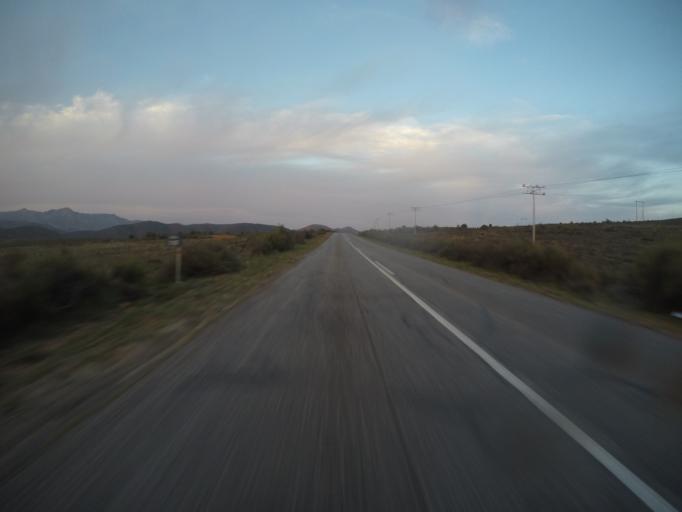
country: ZA
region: Western Cape
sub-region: Eden District Municipality
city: Plettenberg Bay
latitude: -33.7429
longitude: 23.4588
